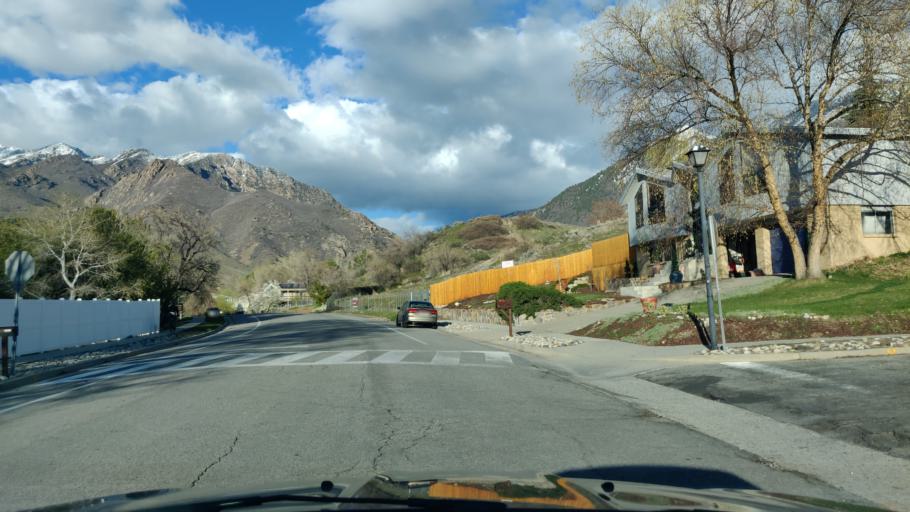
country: US
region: Utah
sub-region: Salt Lake County
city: Cottonwood Heights
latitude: 40.6163
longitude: -111.8065
